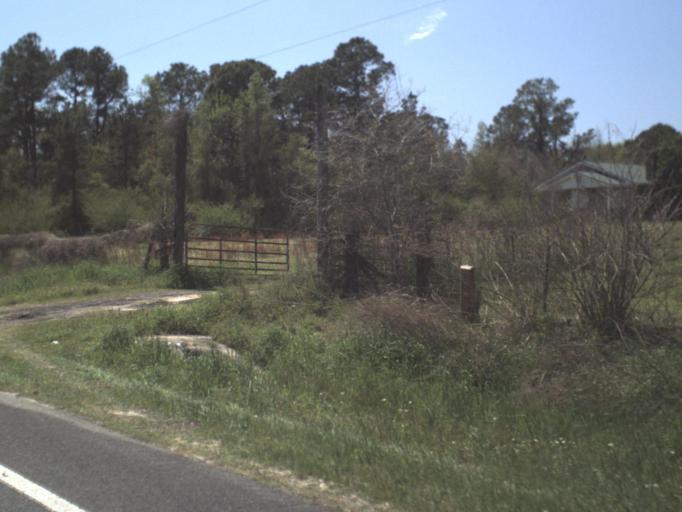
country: US
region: Florida
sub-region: Walton County
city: DeFuniak Springs
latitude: 30.8311
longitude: -85.9544
